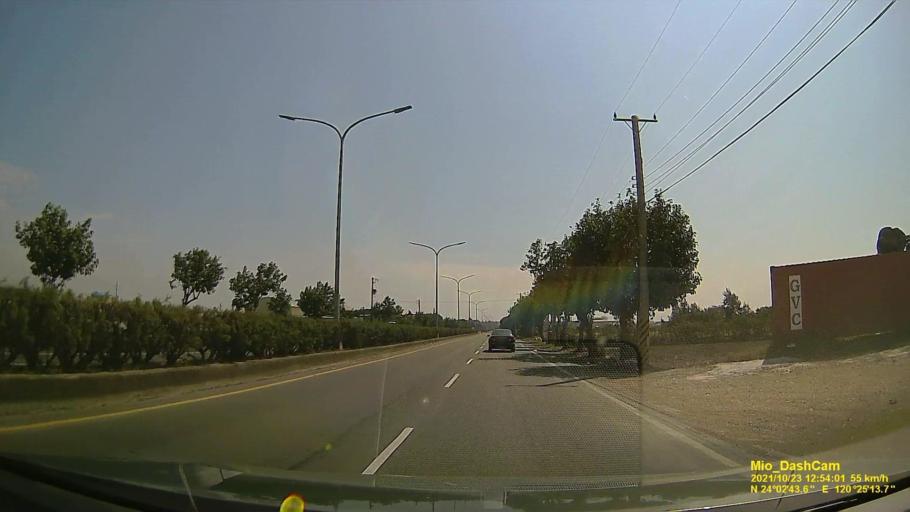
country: TW
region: Taiwan
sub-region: Changhua
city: Chang-hua
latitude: 24.0454
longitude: 120.4204
